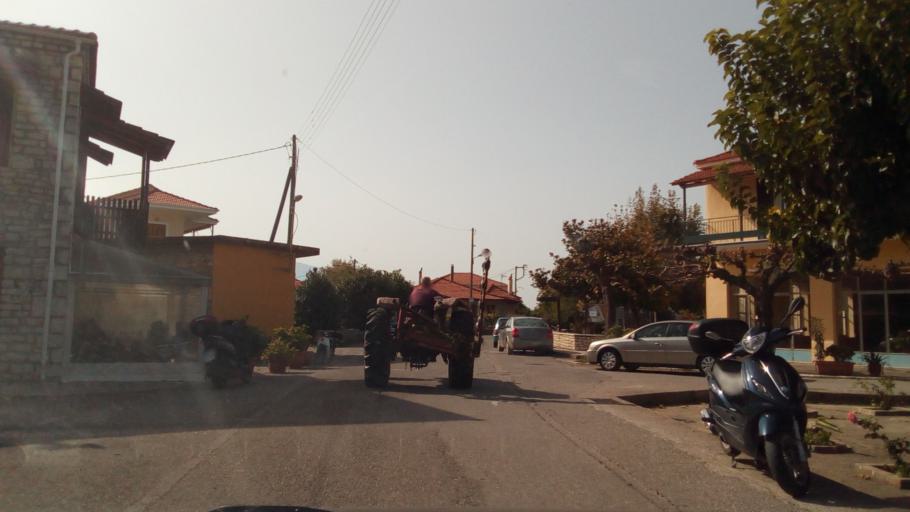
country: GR
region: West Greece
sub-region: Nomos Aitolias kai Akarnanias
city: Nafpaktos
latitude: 38.3962
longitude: 21.8956
